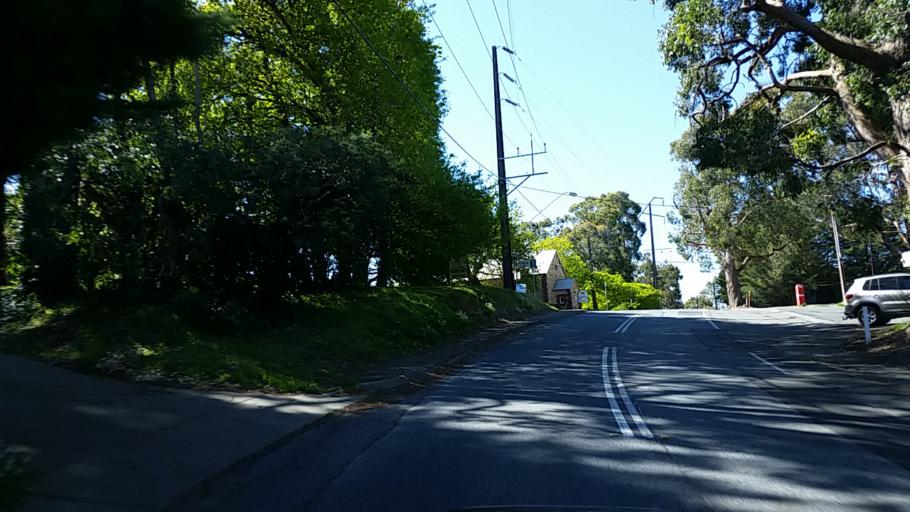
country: AU
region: South Australia
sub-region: Adelaide Hills
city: Bridgewater
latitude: -34.9830
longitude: 138.7257
